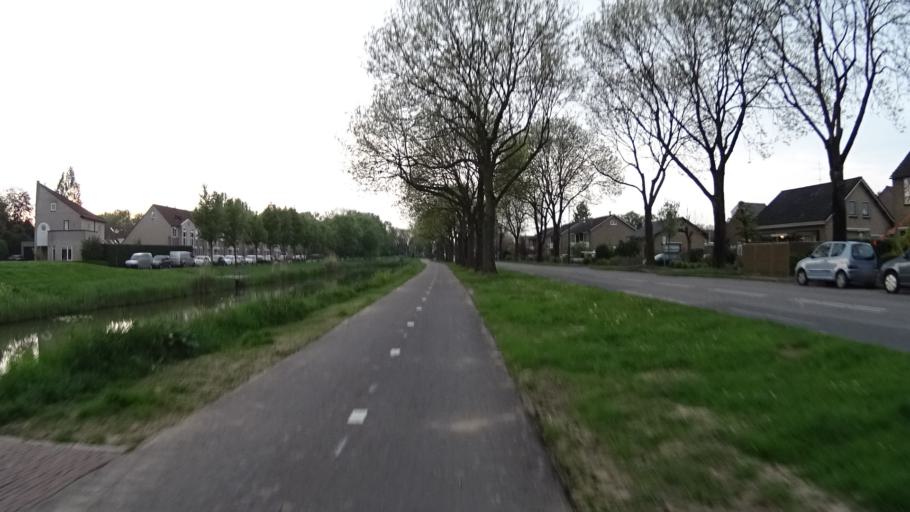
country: NL
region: North Brabant
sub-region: Gemeente Woudrichem
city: Woudrichem
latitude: 51.7960
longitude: 5.0240
